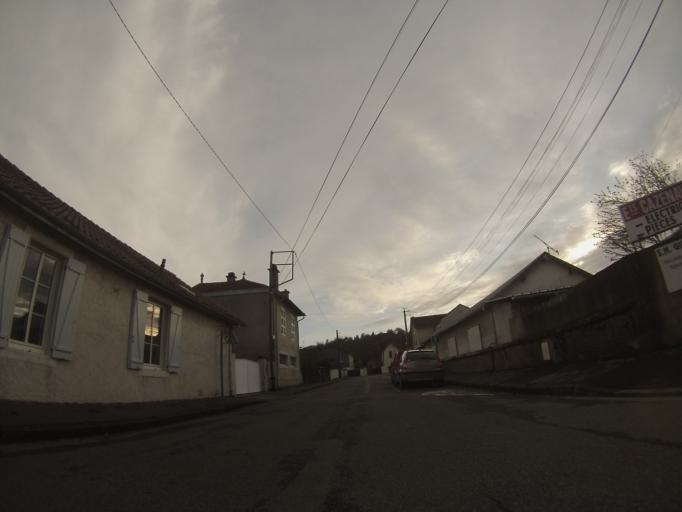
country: FR
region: Aquitaine
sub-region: Departement des Pyrenees-Atlantiques
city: Jurancon
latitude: 43.2853
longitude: -0.3807
